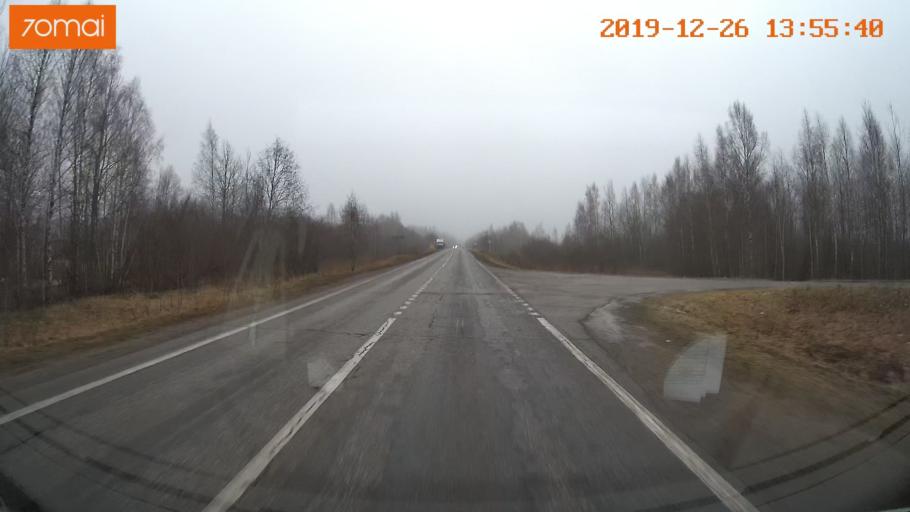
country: RU
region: Jaroslavl
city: Poshekhon'ye
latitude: 58.6008
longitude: 38.6497
